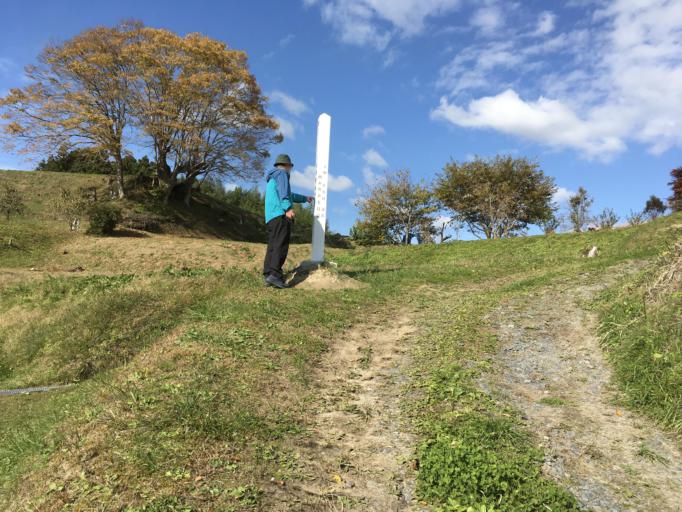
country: JP
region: Iwate
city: Ichinoseki
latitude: 38.9599
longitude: 141.3574
